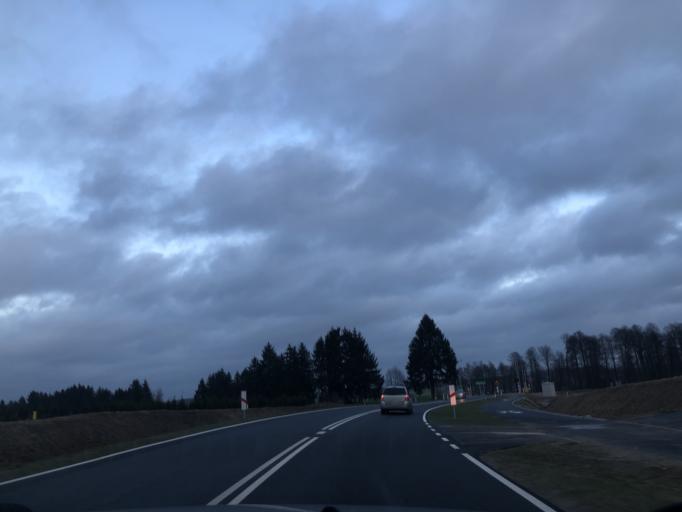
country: PL
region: Podlasie
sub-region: Lomza
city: Lomza
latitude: 53.1247
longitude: 22.0441
